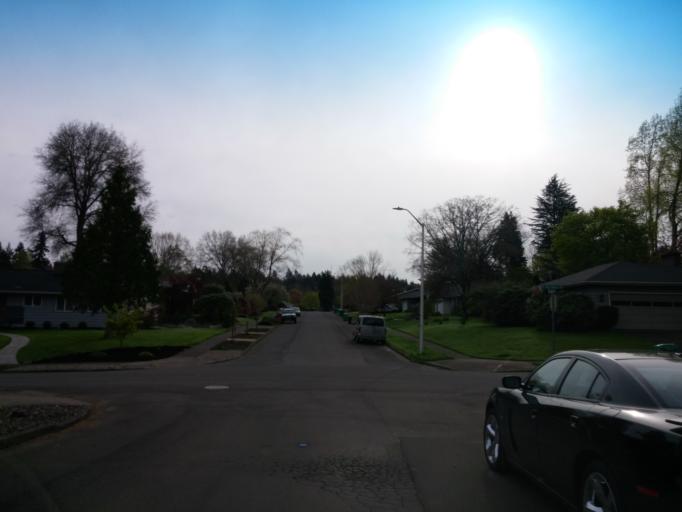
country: US
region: Oregon
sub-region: Washington County
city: Cedar Hills
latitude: 45.5098
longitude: -122.8027
